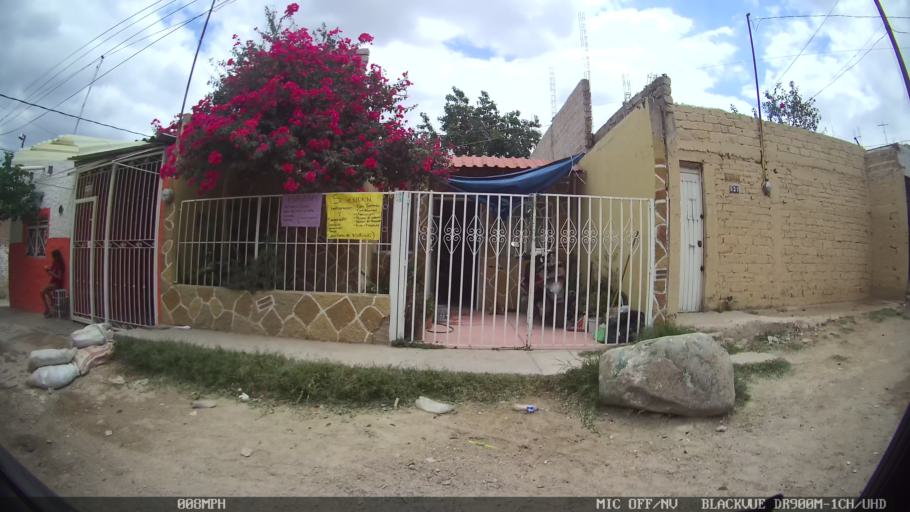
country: MX
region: Jalisco
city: Tonala
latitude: 20.6383
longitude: -103.2605
